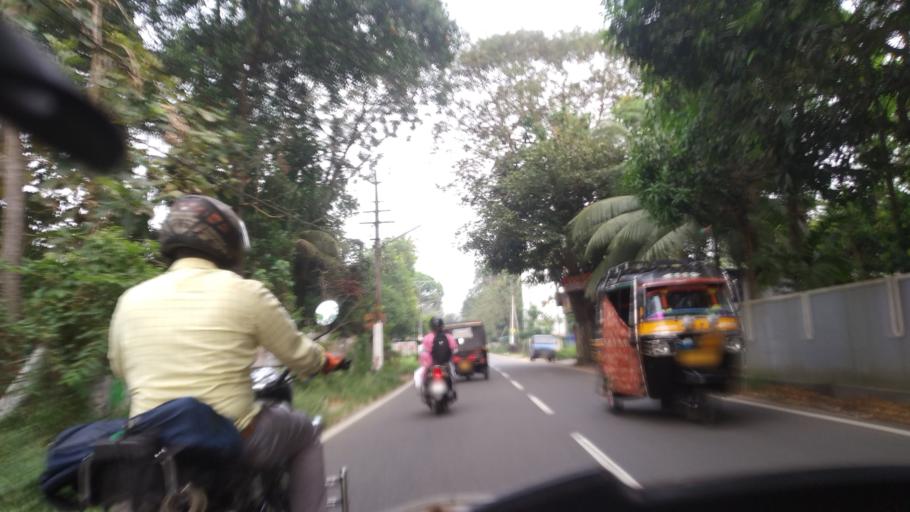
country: IN
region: Kerala
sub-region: Ernakulam
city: Elur
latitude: 10.1498
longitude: 76.2601
